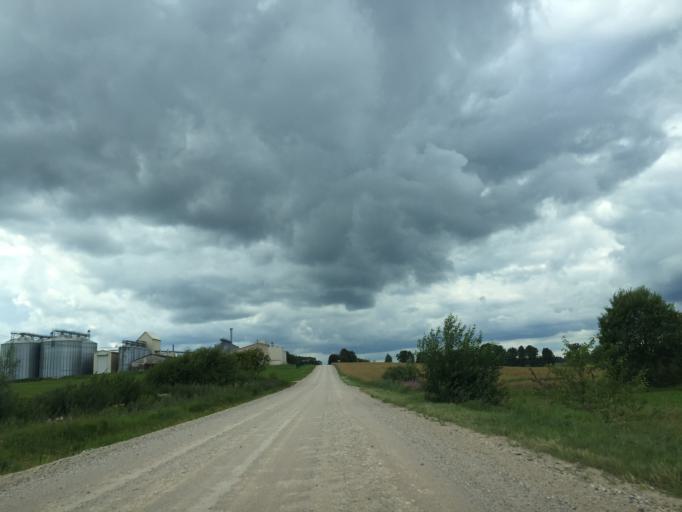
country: LV
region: Malpils
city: Malpils
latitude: 56.8563
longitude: 25.0353
